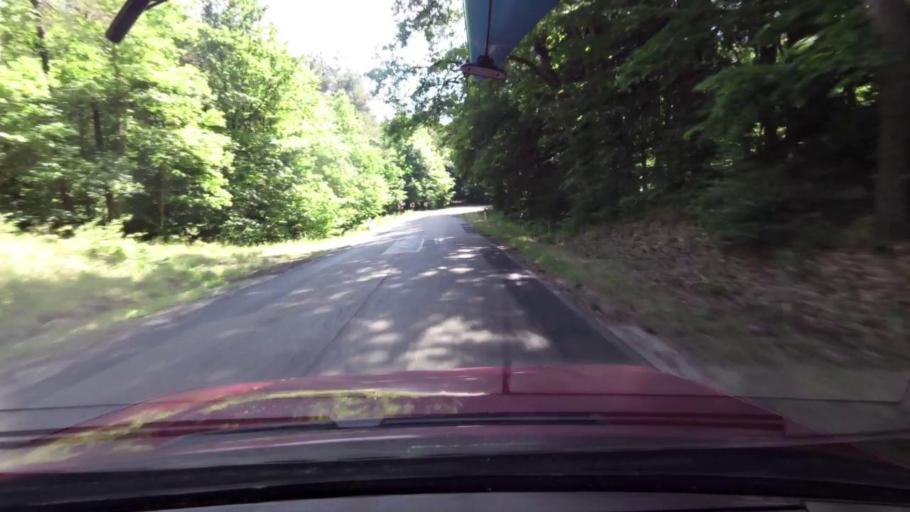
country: PL
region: Pomeranian Voivodeship
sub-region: Powiat slupski
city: Kepice
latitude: 54.2407
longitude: 16.8969
